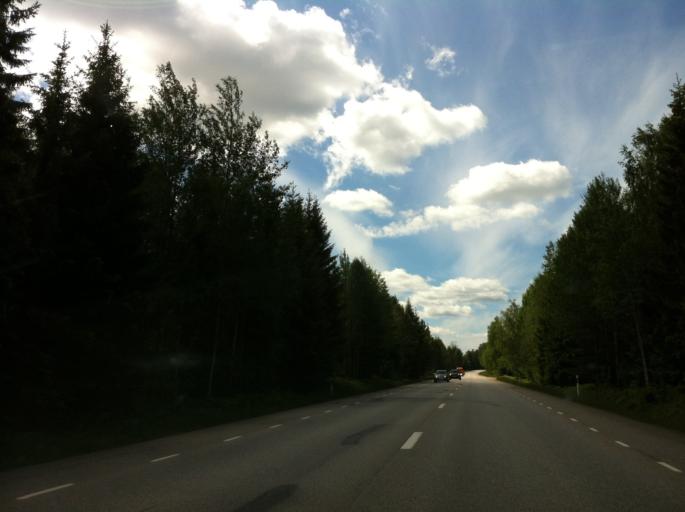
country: SE
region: Vaestra Goetaland
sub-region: Amals Kommun
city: Amal
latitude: 58.9964
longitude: 12.6787
